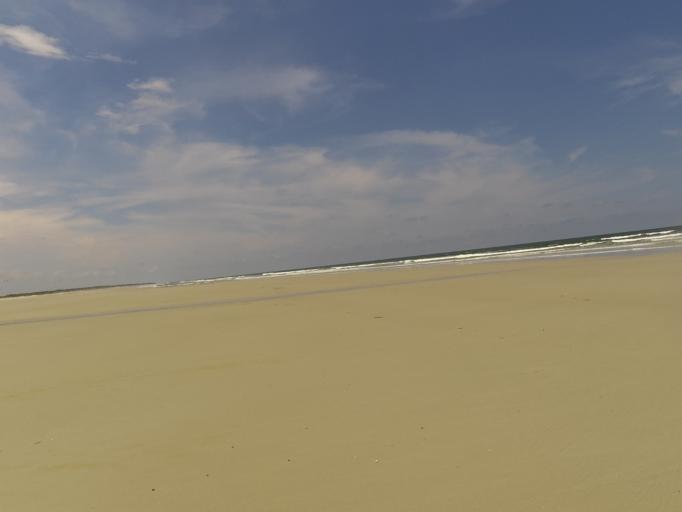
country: US
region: Florida
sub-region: Duval County
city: Atlantic Beach
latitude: 30.4375
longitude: -81.4068
